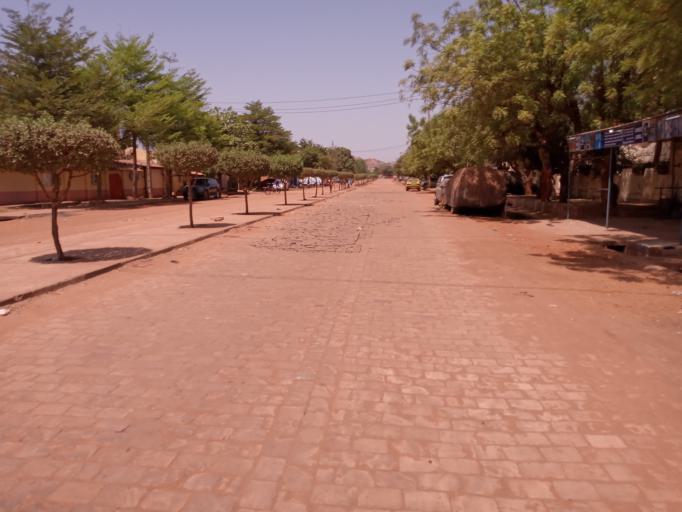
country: ML
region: Bamako
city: Bamako
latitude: 12.6638
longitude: -7.9495
